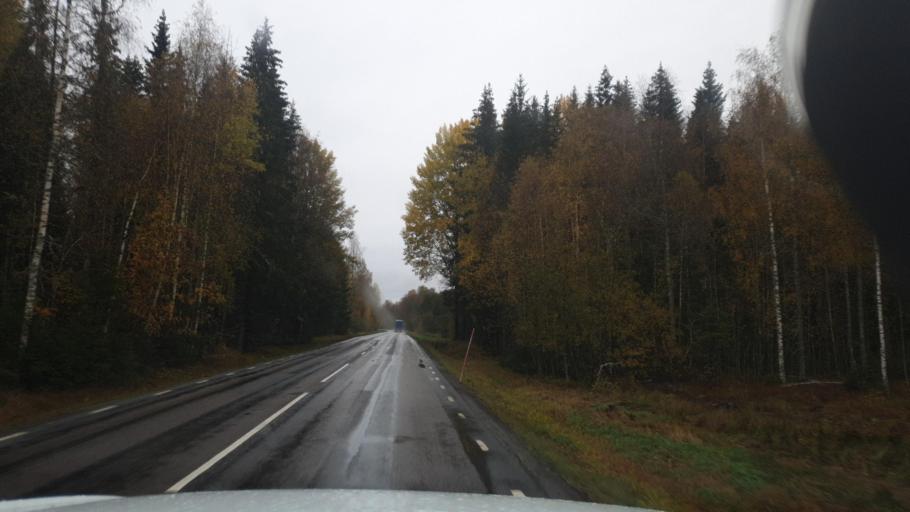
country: SE
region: Vaermland
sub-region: Eda Kommun
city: Charlottenberg
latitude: 59.8316
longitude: 12.2650
